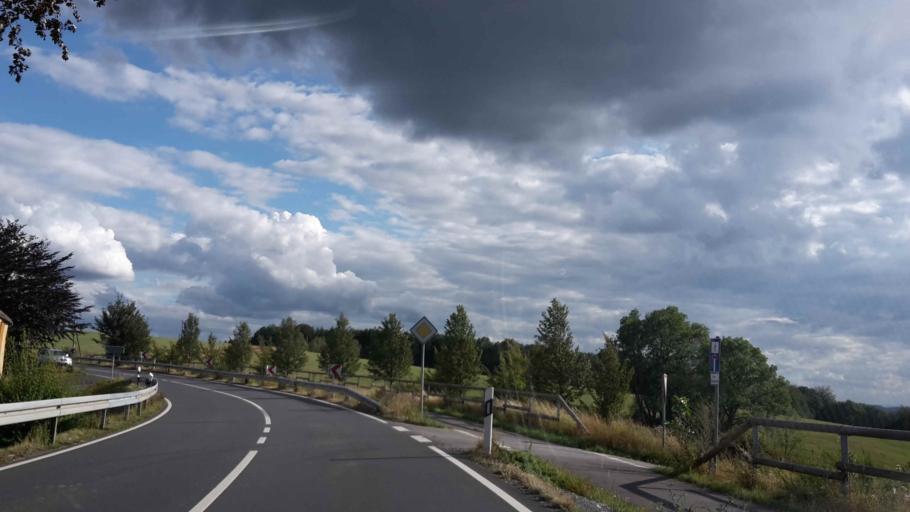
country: DE
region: North Rhine-Westphalia
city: Radevormwald
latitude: 51.1984
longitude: 7.4141
